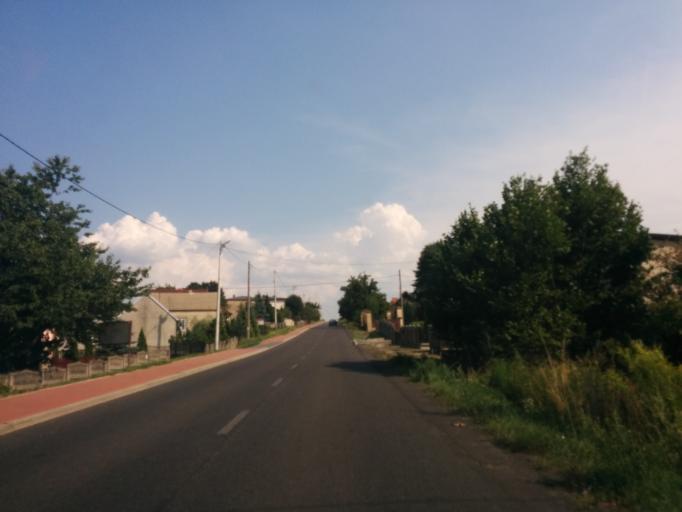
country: PL
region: Silesian Voivodeship
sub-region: Powiat myszkowski
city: Choron
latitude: 50.7126
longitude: 19.2640
